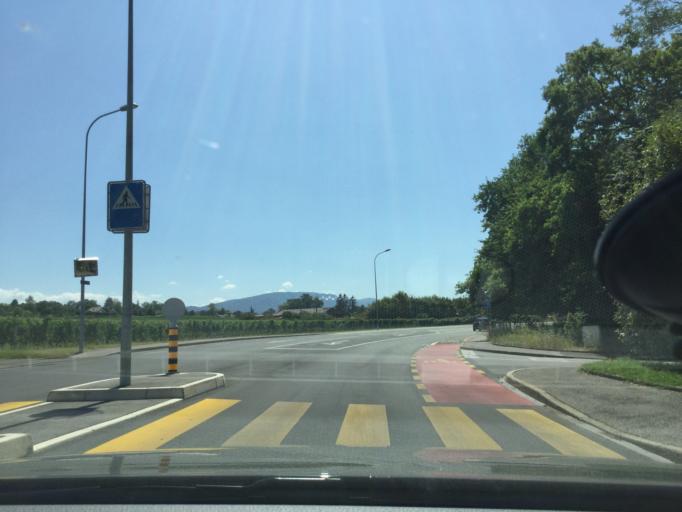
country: CH
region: Geneva
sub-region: Geneva
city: Corsier
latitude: 46.2599
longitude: 6.2124
